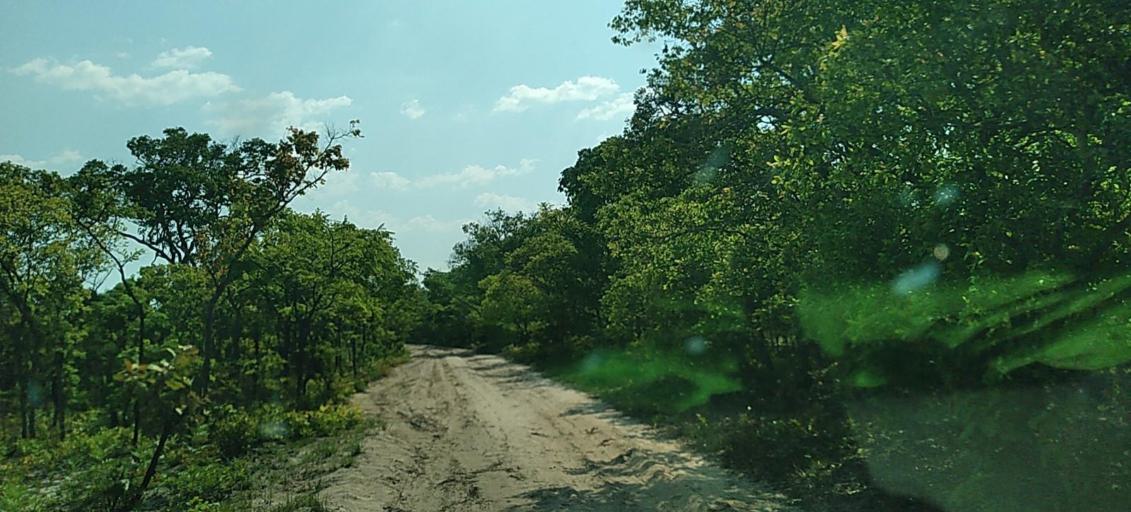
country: ZM
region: North-Western
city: Mwinilunga
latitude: -11.2772
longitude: 24.9290
